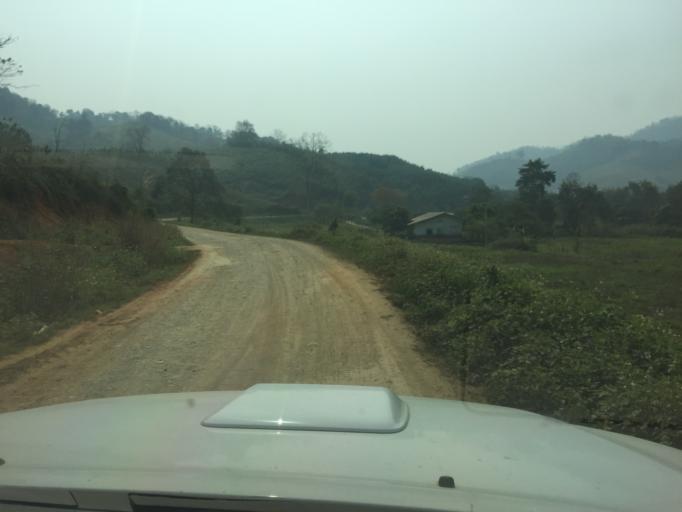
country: TH
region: Phayao
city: Phu Sang
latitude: 19.6161
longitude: 100.5361
